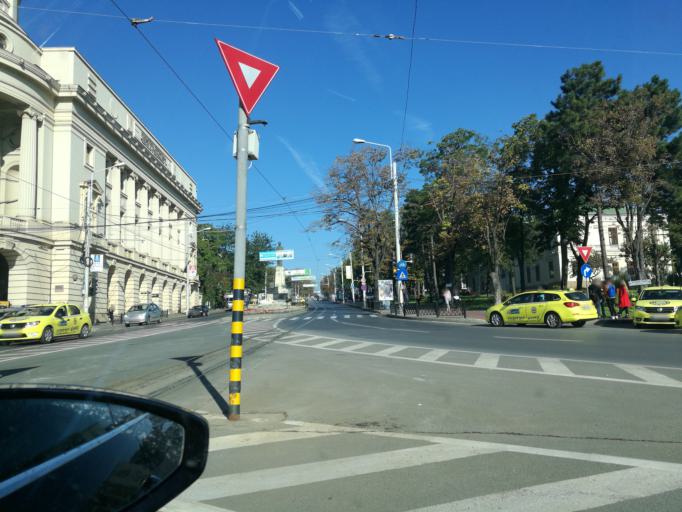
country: RO
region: Iasi
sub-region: Municipiul Iasi
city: Iasi
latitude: 47.1699
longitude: 27.5765
